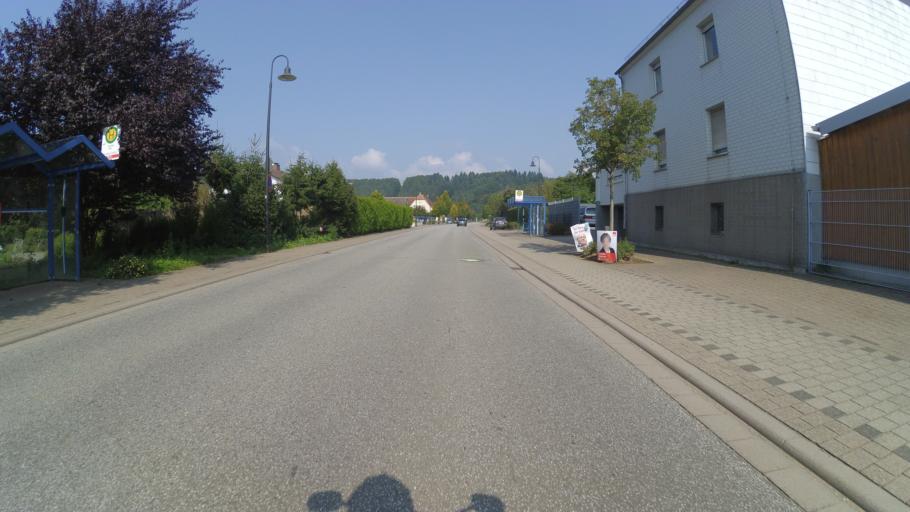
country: DE
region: Rheinland-Pfalz
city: Contwig
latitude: 49.2544
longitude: 7.4207
